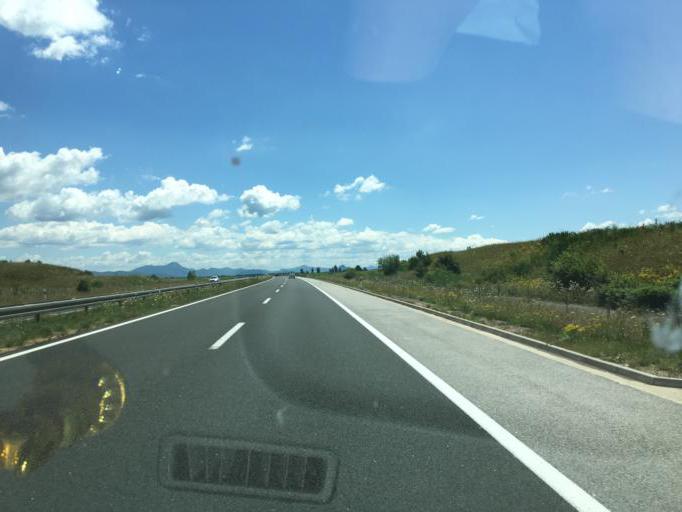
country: HR
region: Licko-Senjska
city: Gospic
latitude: 44.5243
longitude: 15.4573
